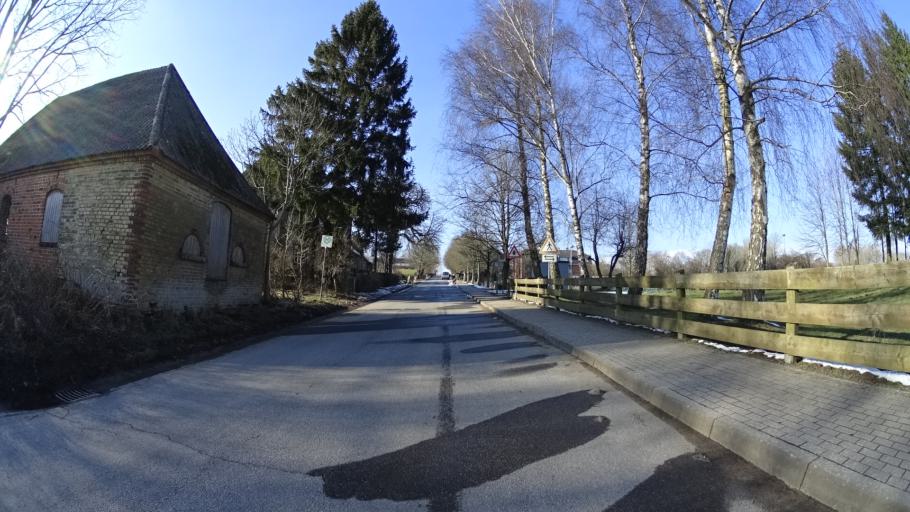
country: DE
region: Schleswig-Holstein
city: Martensrade
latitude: 54.2725
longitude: 10.3912
